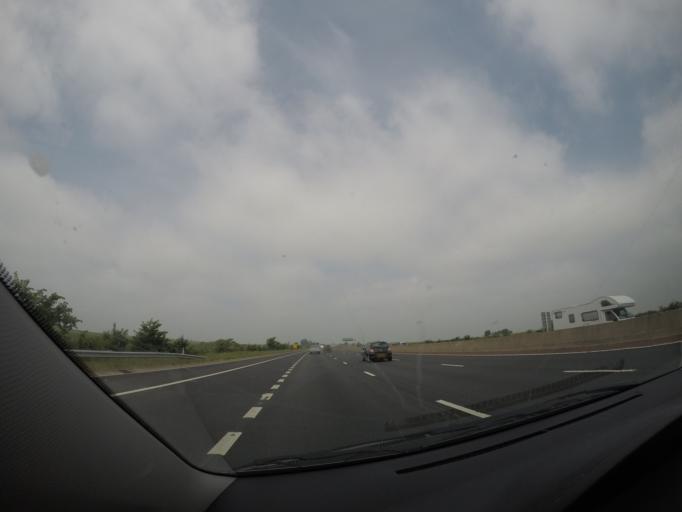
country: GB
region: England
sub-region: North Yorkshire
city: Boroughbridge
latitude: 54.1531
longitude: -1.4394
